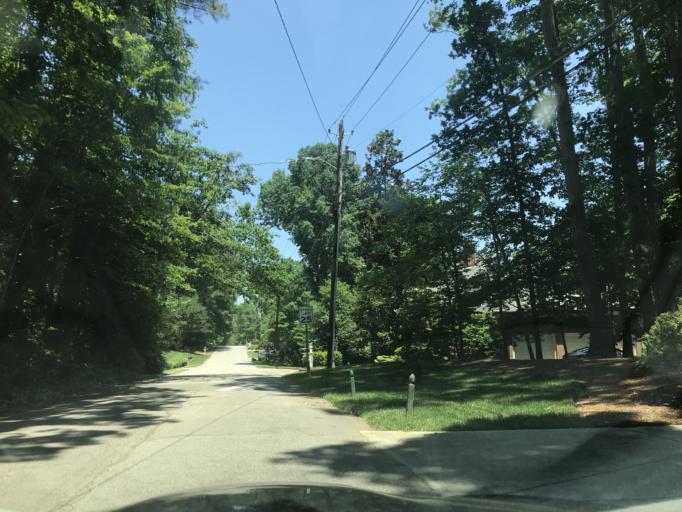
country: US
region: North Carolina
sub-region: Wake County
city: West Raleigh
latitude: 35.8280
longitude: -78.6571
